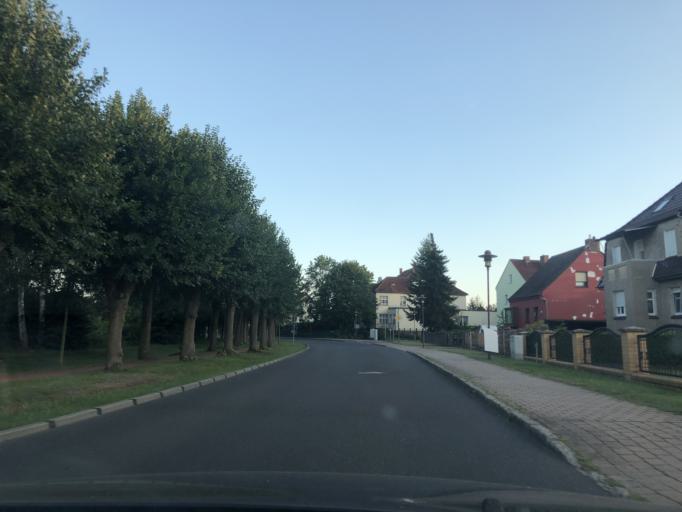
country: DE
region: Brandenburg
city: Mullrose
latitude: 52.2379
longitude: 14.4122
